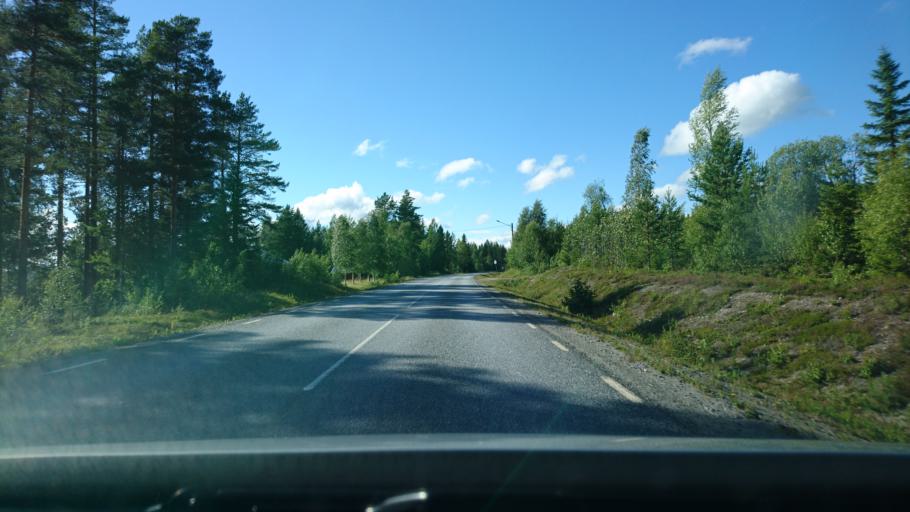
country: SE
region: Vaesterbotten
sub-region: Asele Kommun
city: Asele
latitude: 64.3442
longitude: 17.0063
